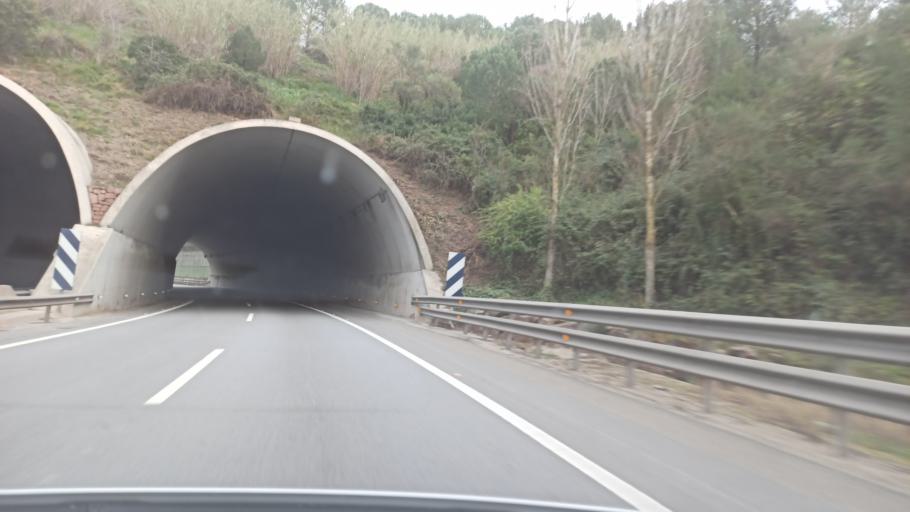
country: ES
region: Catalonia
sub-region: Provincia de Barcelona
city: Cervello
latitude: 41.3901
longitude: 1.9628
